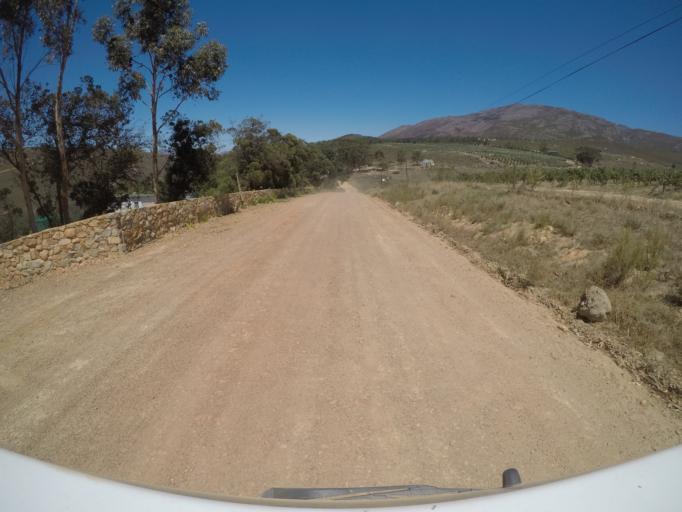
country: ZA
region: Western Cape
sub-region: Overberg District Municipality
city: Caledon
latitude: -34.1785
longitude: 19.2249
